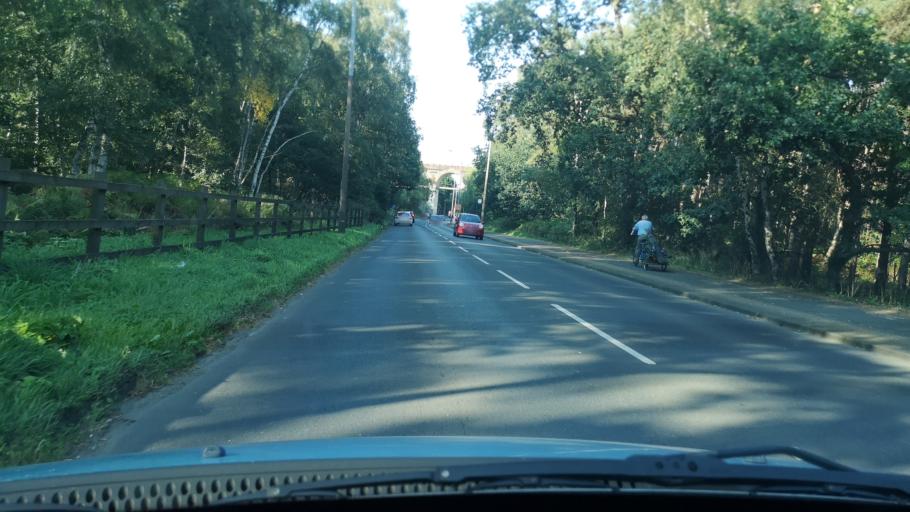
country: GB
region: England
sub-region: North Lincolnshire
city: Scunthorpe
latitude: 53.5828
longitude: -0.6842
